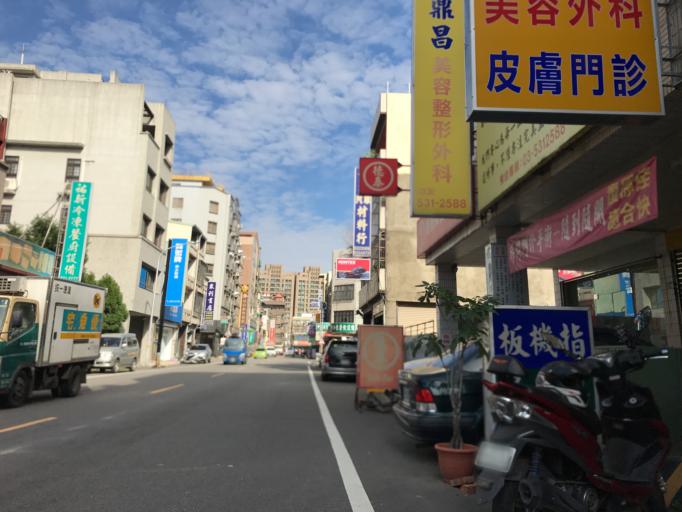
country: TW
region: Taiwan
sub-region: Hsinchu
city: Hsinchu
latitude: 24.8100
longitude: 120.9807
